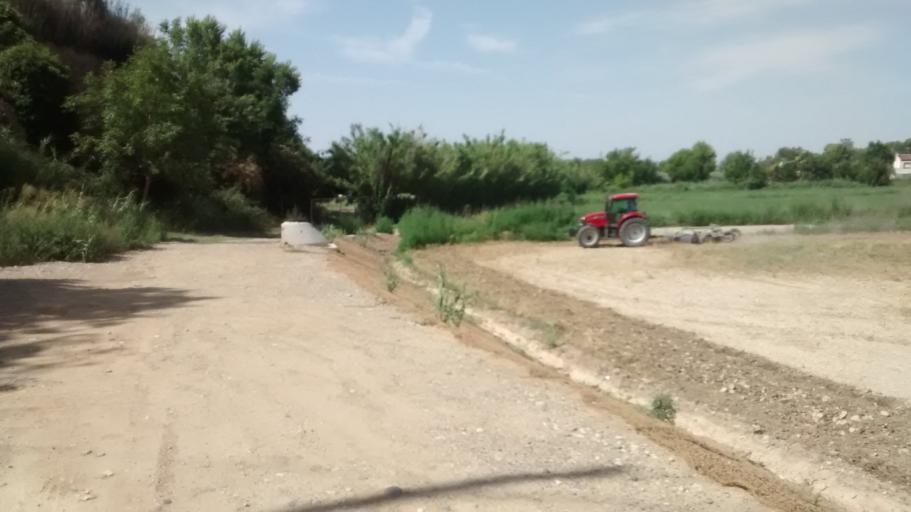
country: ES
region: Aragon
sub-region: Provincia de Zaragoza
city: Villanueva de Gallego
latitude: 41.7617
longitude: -0.7995
